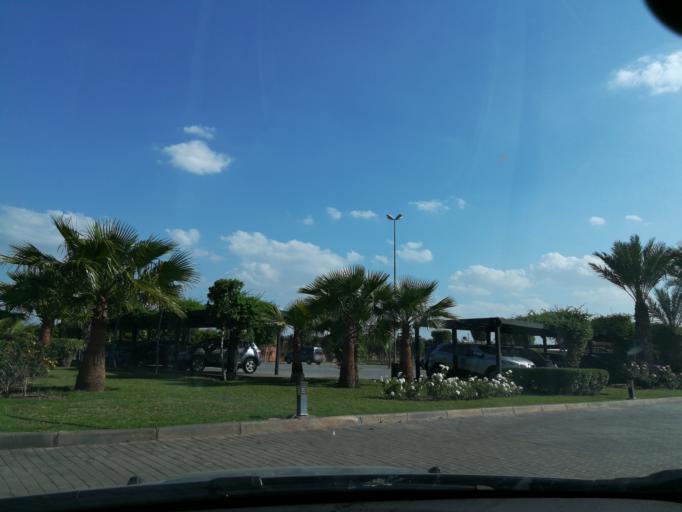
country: MA
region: Marrakech-Tensift-Al Haouz
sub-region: Marrakech
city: Marrakesh
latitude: 31.6692
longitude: -8.0593
